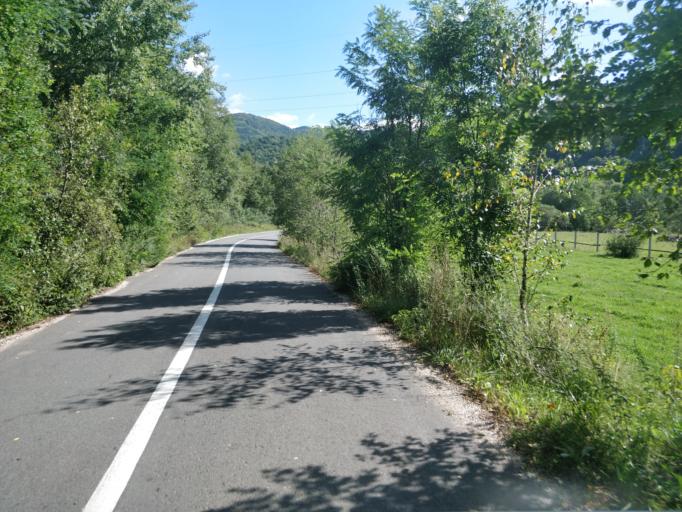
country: RO
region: Cluj
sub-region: Comuna Sacueu
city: Sacuieu
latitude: 46.8030
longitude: 22.8883
